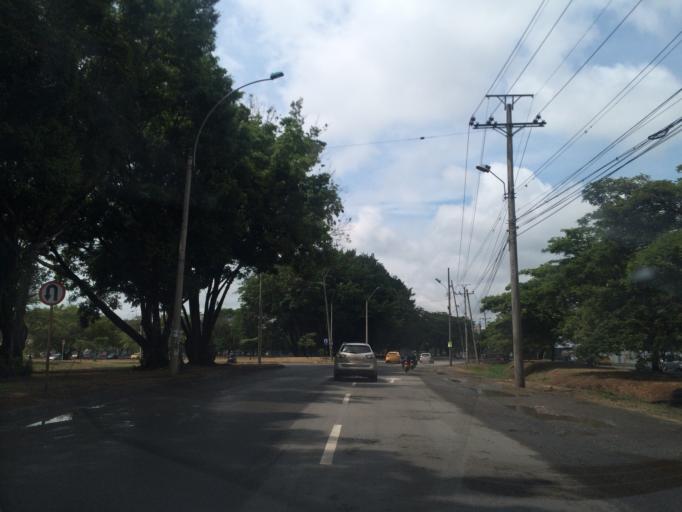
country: CO
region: Valle del Cauca
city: Cali
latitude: 3.3706
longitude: -76.5253
